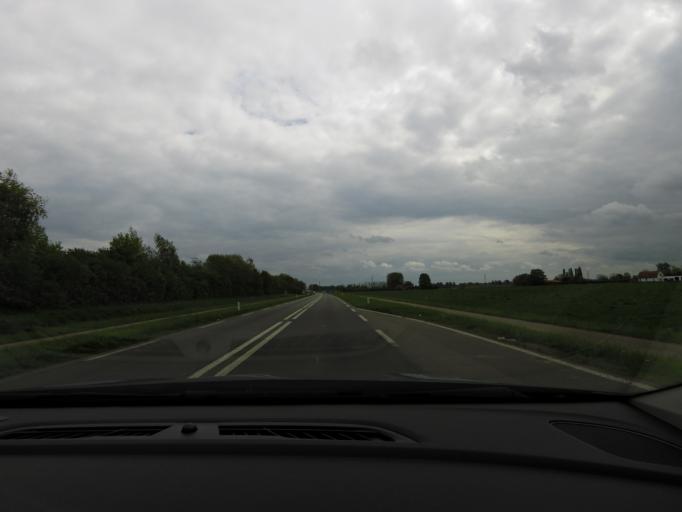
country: NL
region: Gelderland
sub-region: Gemeente Tiel
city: Tiel
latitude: 51.8980
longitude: 5.3742
